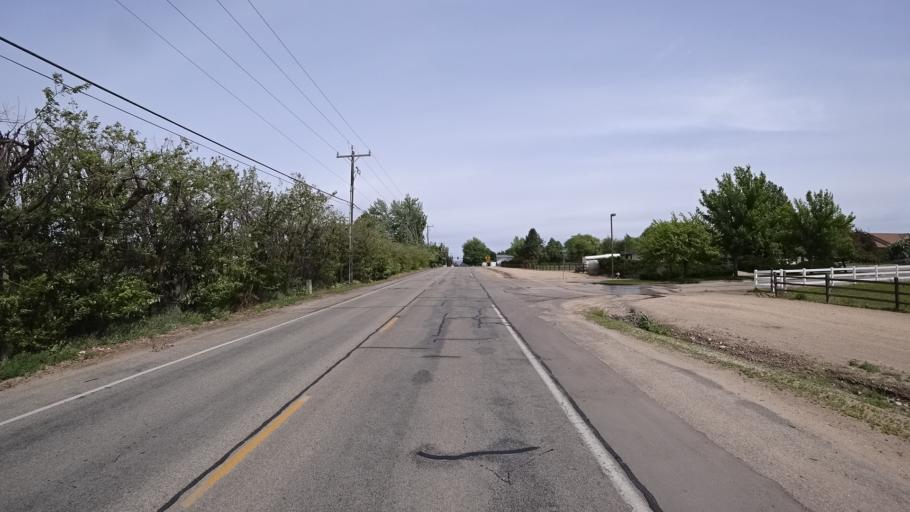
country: US
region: Idaho
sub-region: Ada County
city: Meridian
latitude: 43.5589
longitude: -116.3143
